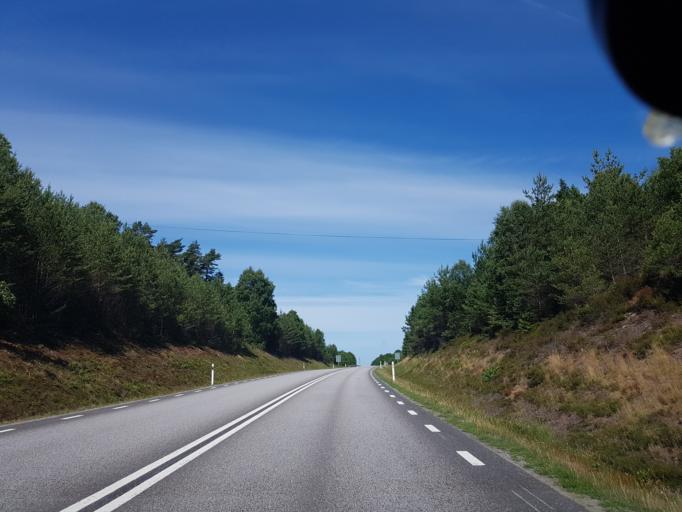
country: SE
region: Vaestra Goetaland
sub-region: Lysekils Kommun
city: Lysekil
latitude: 58.1583
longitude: 11.5030
